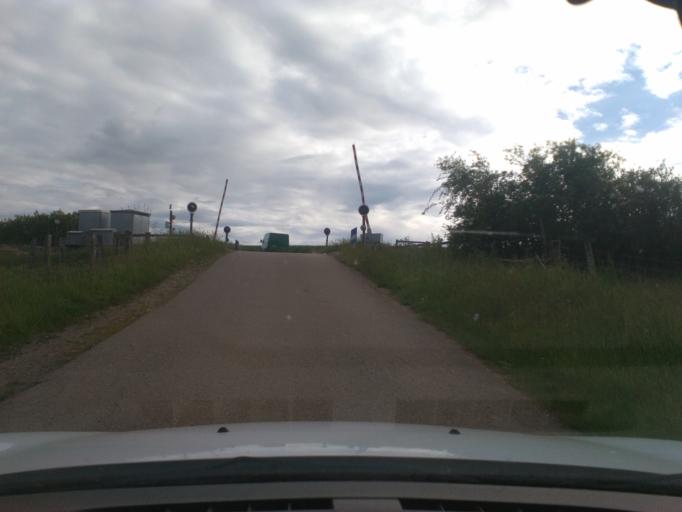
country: FR
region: Lorraine
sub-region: Departement des Vosges
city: Mirecourt
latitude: 48.3423
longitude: 6.1022
